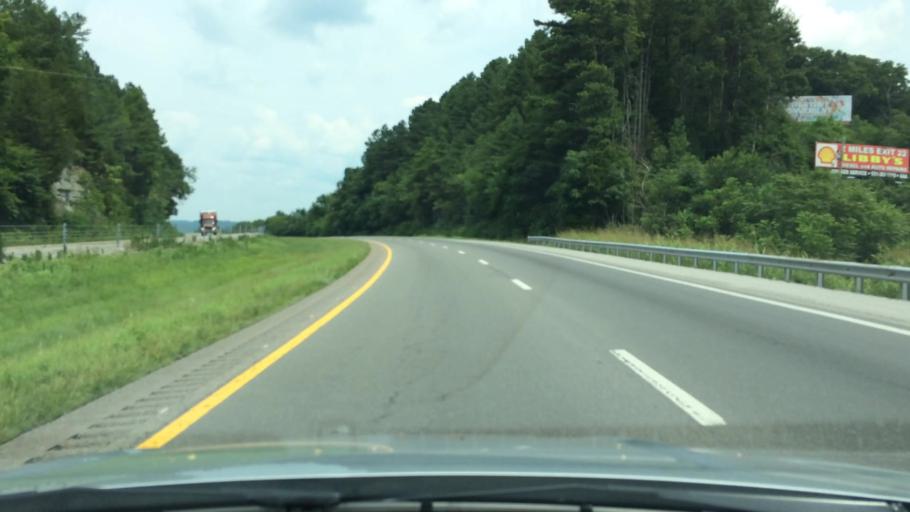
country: US
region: Tennessee
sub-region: Marshall County
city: Cornersville
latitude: 35.2599
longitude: -86.8831
